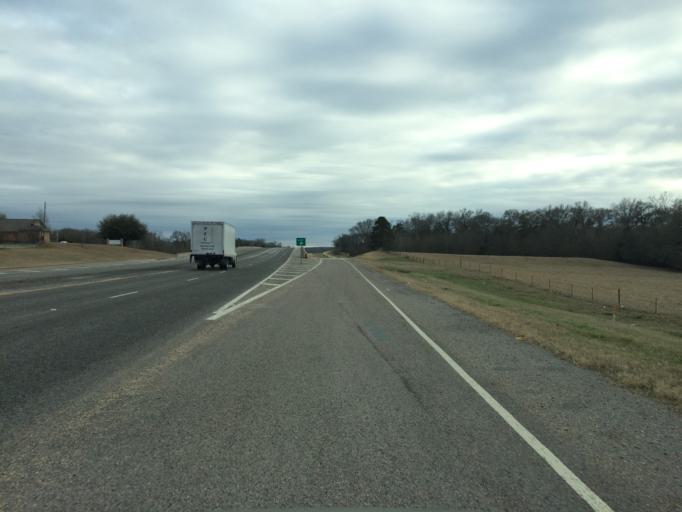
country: US
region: Texas
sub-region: Wood County
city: Mineola
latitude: 32.6413
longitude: -95.4890
